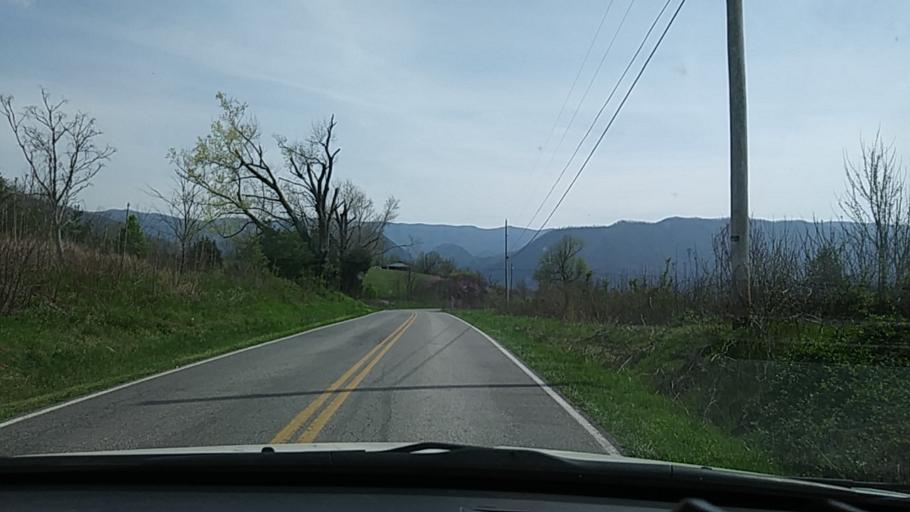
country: US
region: Tennessee
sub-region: Greene County
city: Tusculum
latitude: 36.0927
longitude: -82.7284
